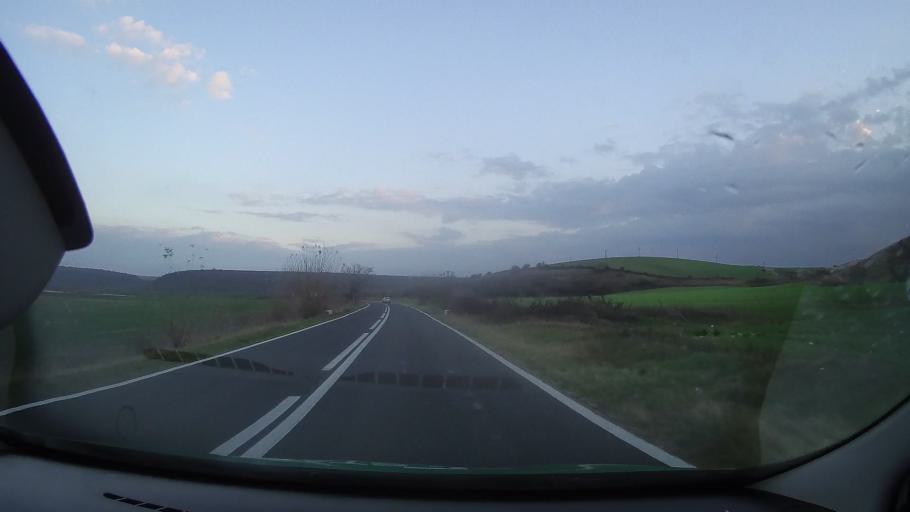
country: RO
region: Constanta
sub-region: Comuna Lipnita
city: Lipnita
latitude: 44.0982
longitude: 27.6307
